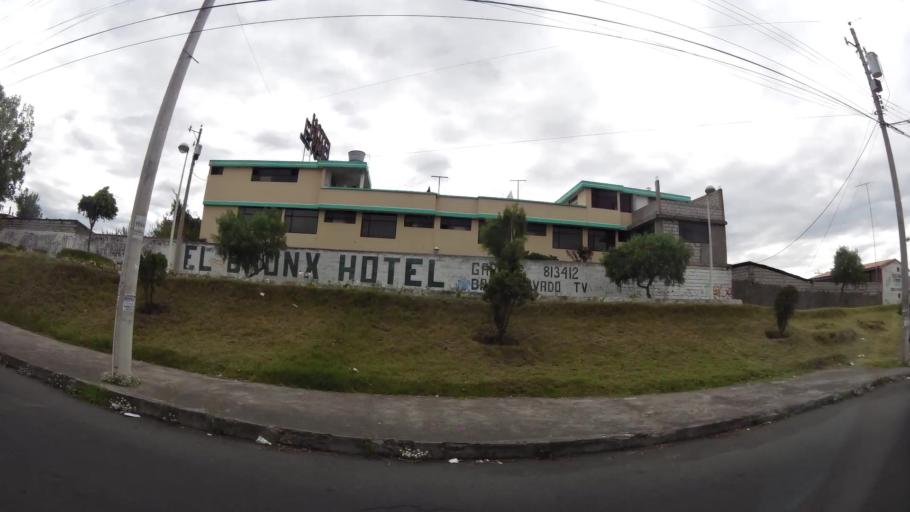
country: EC
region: Cotopaxi
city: Latacunga
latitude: -0.9399
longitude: -78.6171
